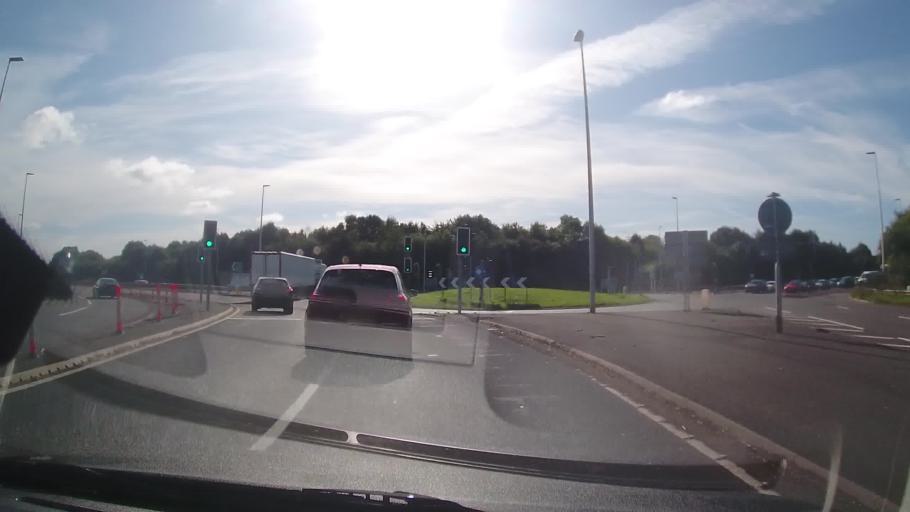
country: GB
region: England
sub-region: Shropshire
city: Shrewsbury
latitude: 52.7068
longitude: -2.7000
